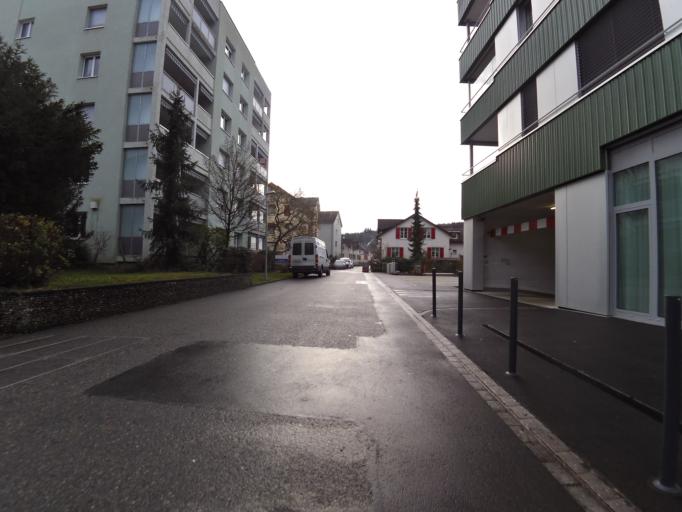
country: CH
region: Thurgau
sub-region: Frauenfeld District
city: Frauenfeld
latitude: 47.5528
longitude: 8.8910
